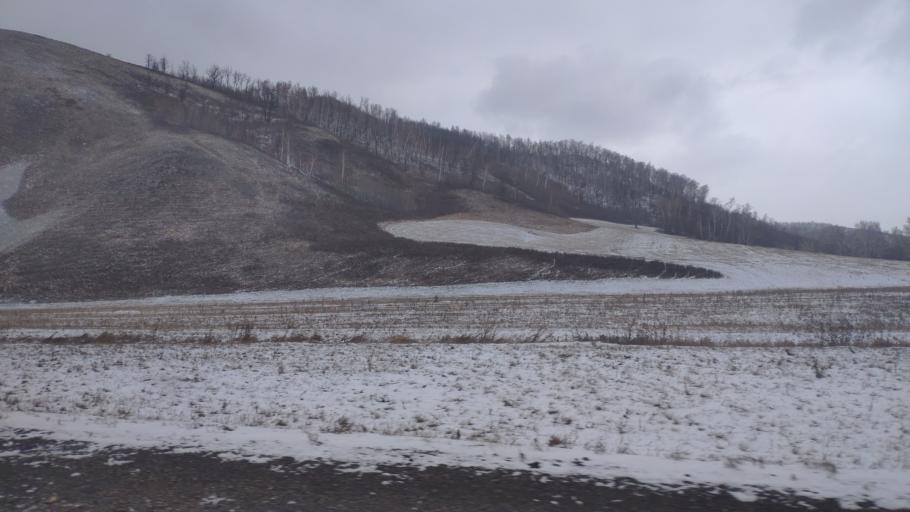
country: RU
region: Bashkortostan
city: Isyangulovo
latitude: 52.1608
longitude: 56.9214
